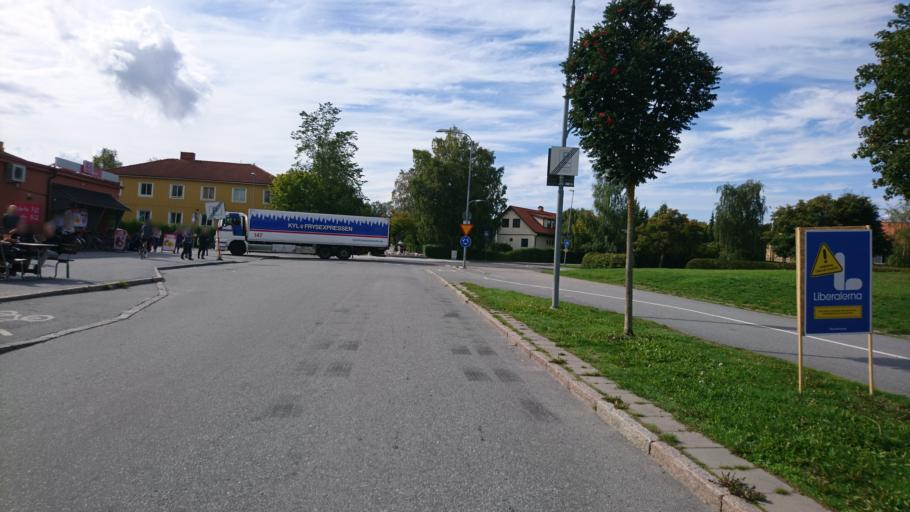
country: SE
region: Uppsala
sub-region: Uppsala Kommun
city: Uppsala
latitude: 59.8463
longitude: 17.6313
